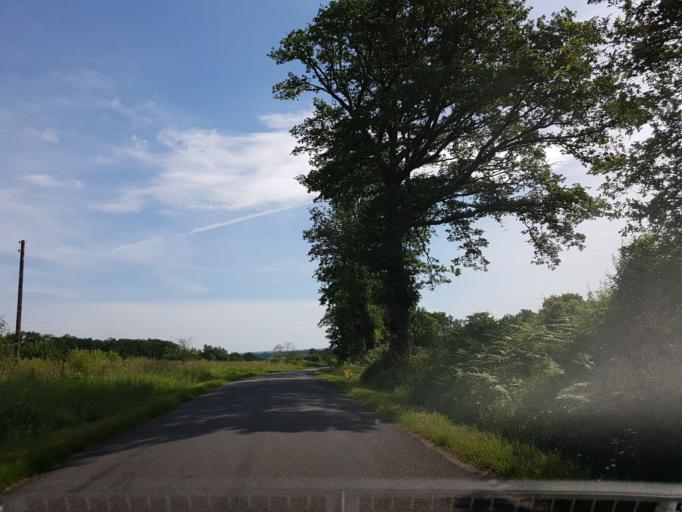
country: FR
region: Poitou-Charentes
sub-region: Departement de la Charente
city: Exideuil
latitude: 45.9181
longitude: 0.6995
